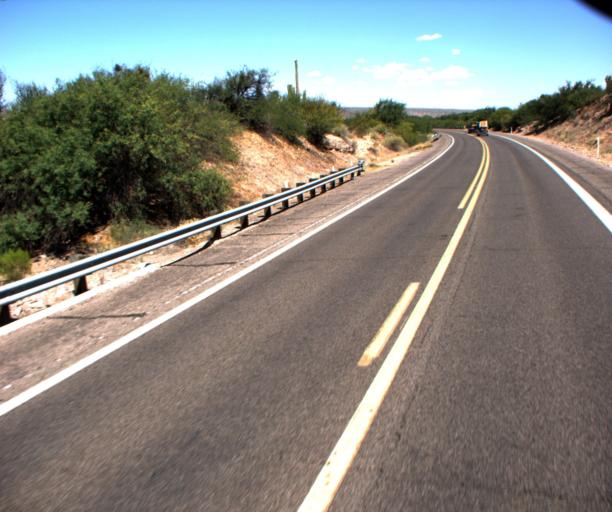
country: US
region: Arizona
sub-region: Pinal County
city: Mammoth
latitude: 32.8294
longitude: -110.7000
